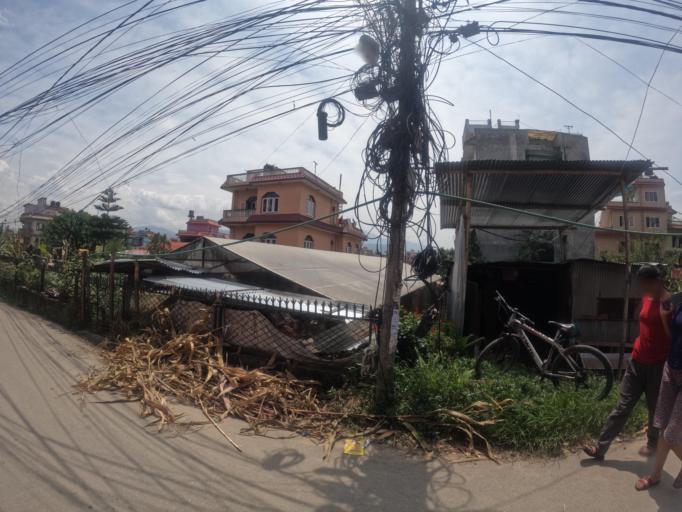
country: NP
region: Central Region
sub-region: Bagmati Zone
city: Kathmandu
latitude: 27.6807
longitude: 85.3676
